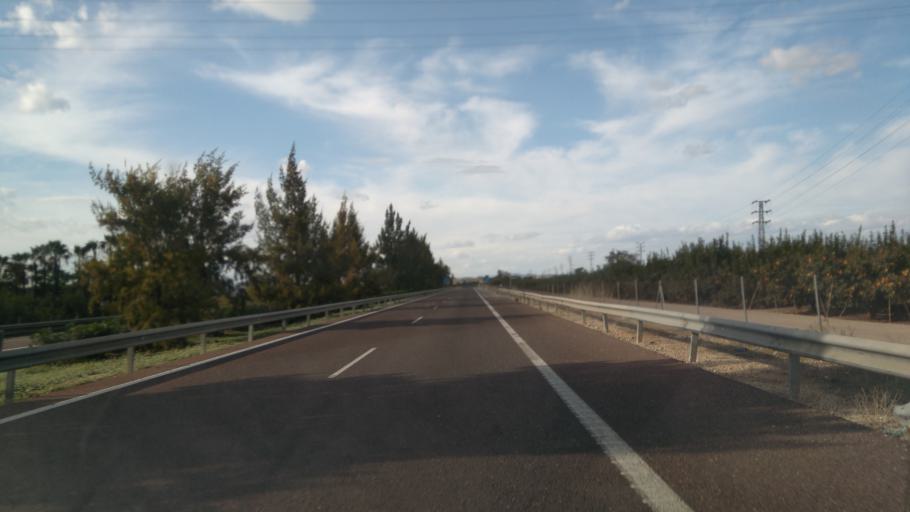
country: ES
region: Valencia
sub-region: Provincia de Valencia
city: L'Alcudia
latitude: 39.1829
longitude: -0.4881
